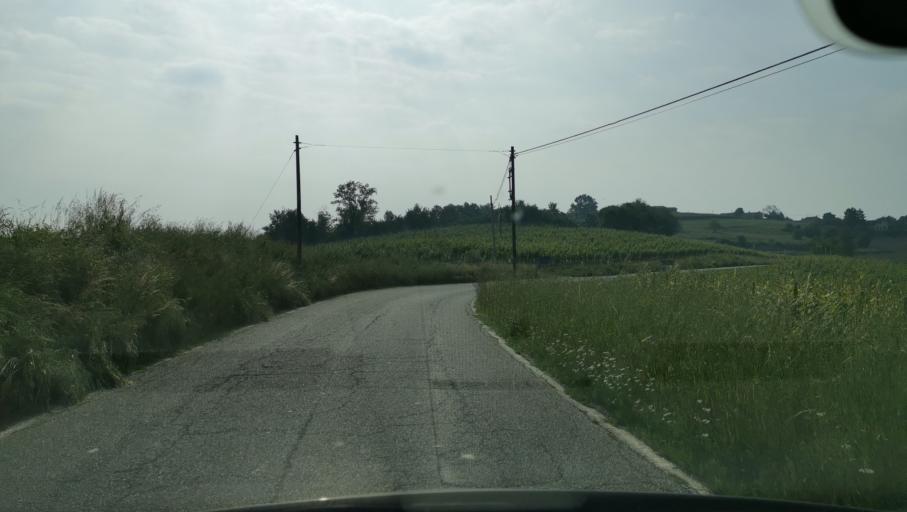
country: IT
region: Piedmont
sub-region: Provincia di Alessandria
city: Odalengo Piccolo
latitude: 45.0700
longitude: 8.2225
